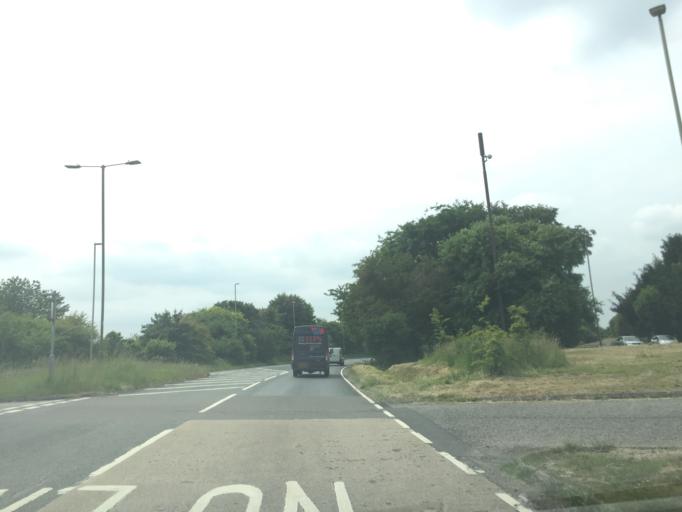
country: GB
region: England
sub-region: Hampshire
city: Kings Worthy
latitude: 51.0579
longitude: -1.2630
